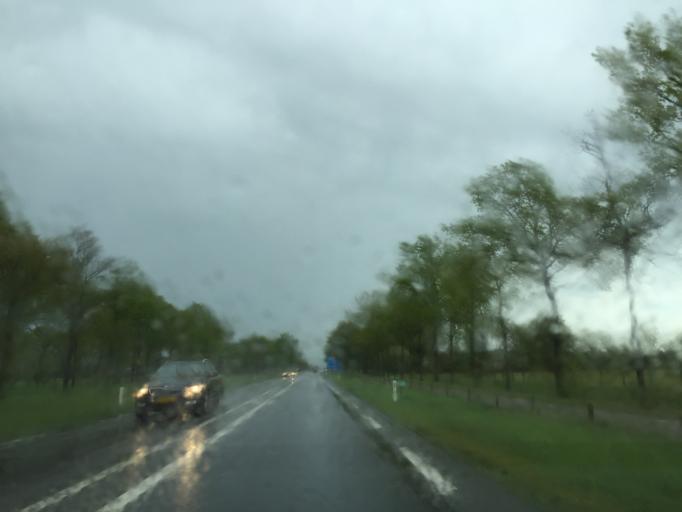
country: NL
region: Overijssel
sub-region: Gemeente Dalfsen
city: Dalfsen
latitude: 52.5275
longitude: 6.2497
